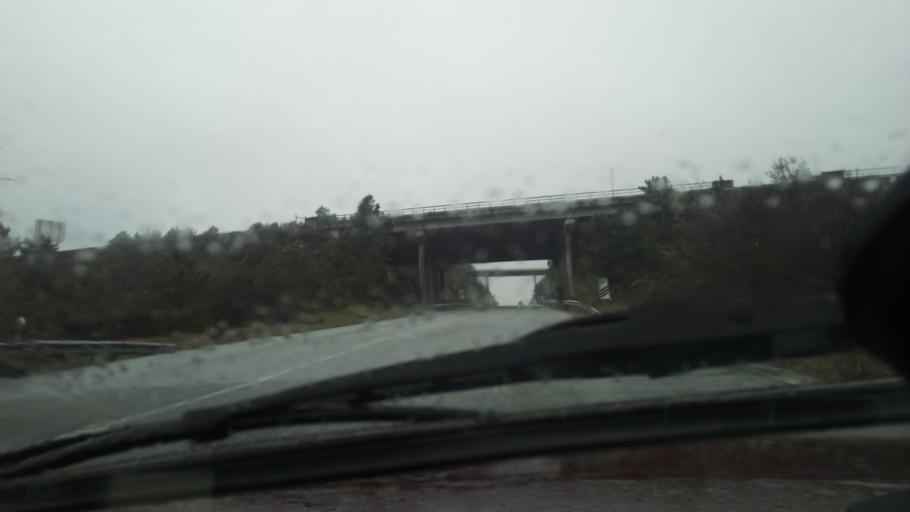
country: PT
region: Guarda
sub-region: Fornos de Algodres
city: Fornos de Algodres
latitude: 40.6164
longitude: -7.6063
